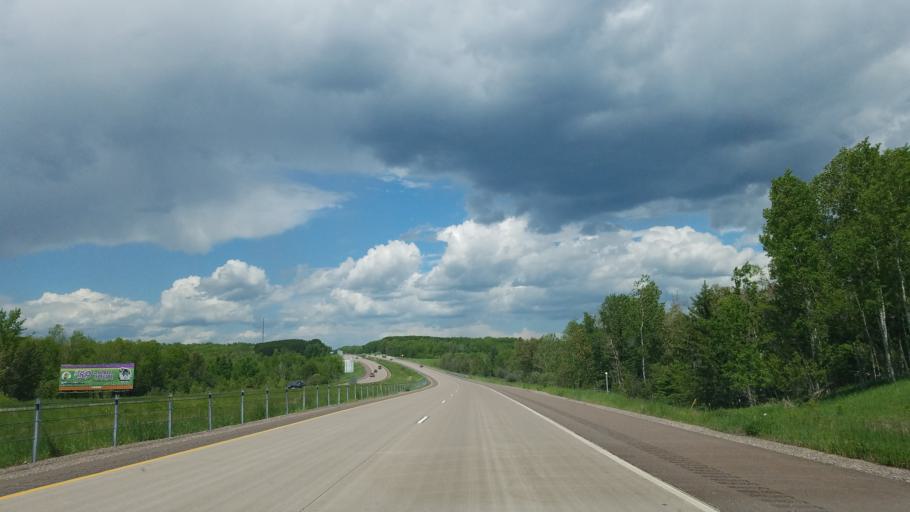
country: US
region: Minnesota
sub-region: Carlton County
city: Moose Lake
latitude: 46.4471
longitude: -92.7359
